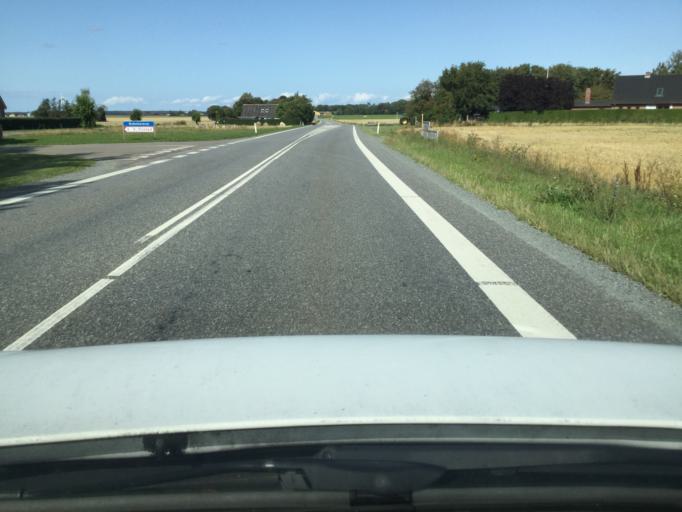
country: DK
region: Zealand
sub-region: Lolland Kommune
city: Rodby
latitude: 54.7205
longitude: 11.3846
